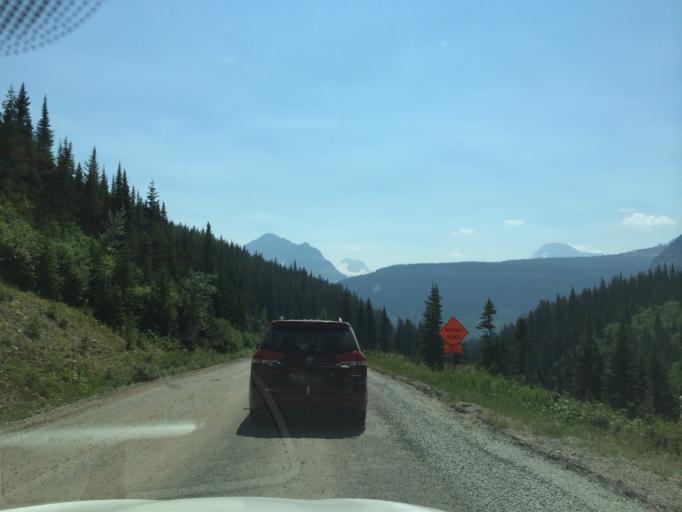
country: US
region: Montana
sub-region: Flathead County
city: Columbia Falls
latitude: 48.6998
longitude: -113.6675
